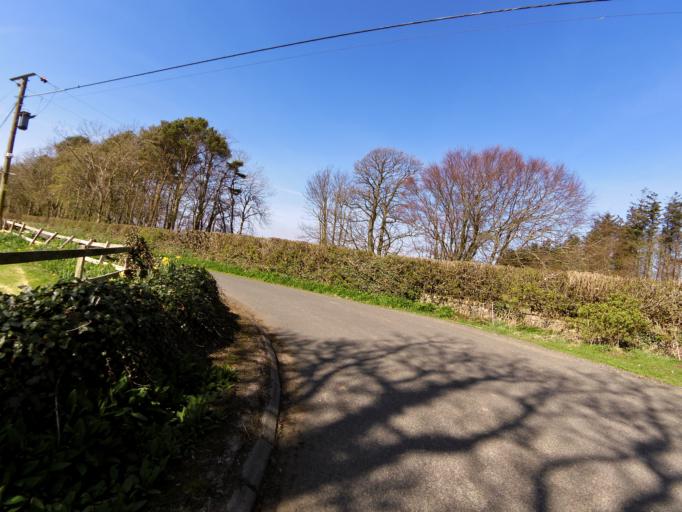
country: GB
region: Scotland
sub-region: Angus
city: Montrose
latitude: 56.6760
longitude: -2.4901
